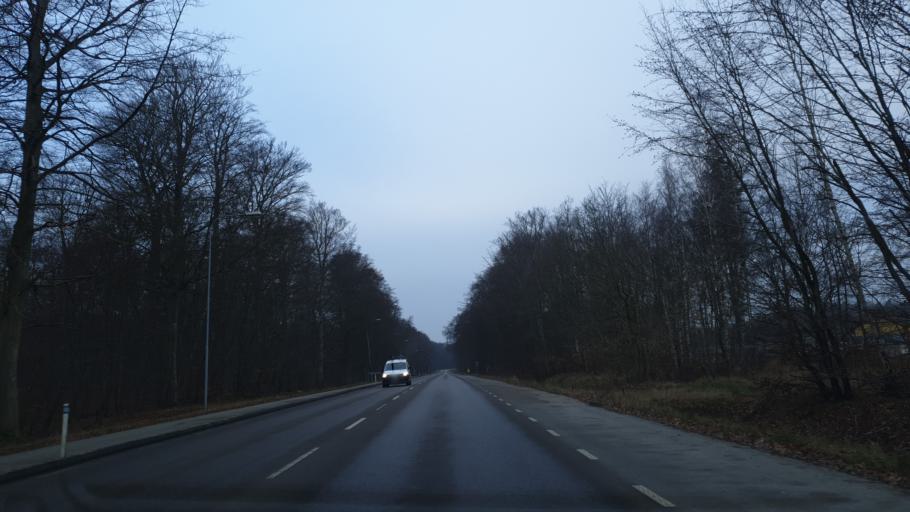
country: SE
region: Blekinge
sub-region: Solvesborgs Kommun
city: Soelvesborg
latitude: 56.0553
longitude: 14.5645
